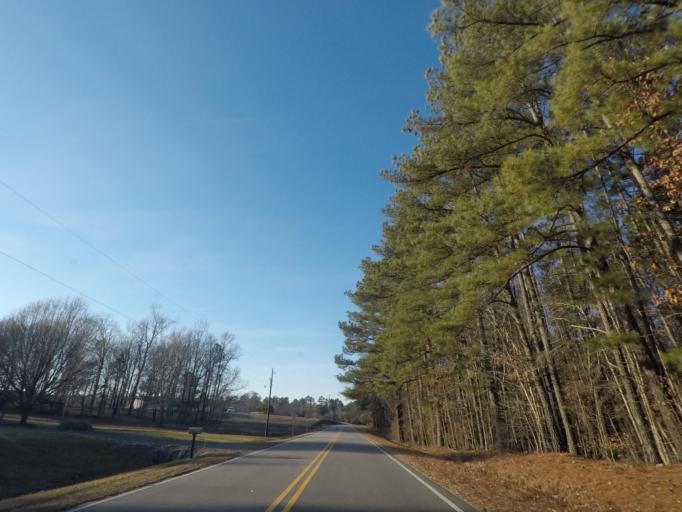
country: US
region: North Carolina
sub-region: Granville County
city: Butner
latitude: 36.0759
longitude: -78.7515
